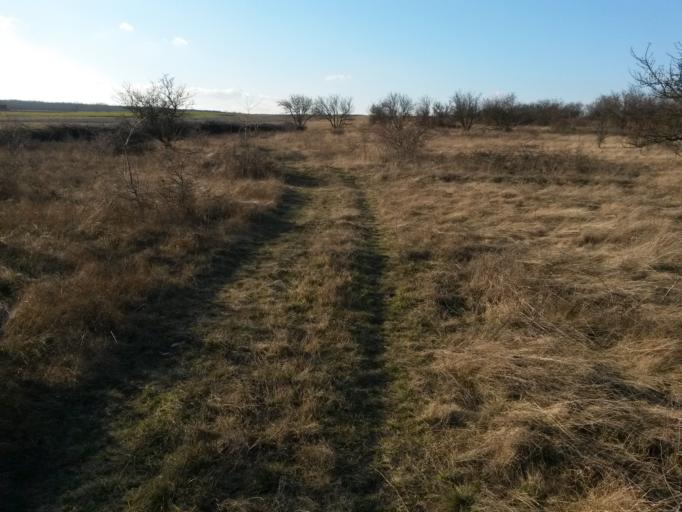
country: HU
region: Pest
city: Perbal
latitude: 47.5880
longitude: 18.7455
